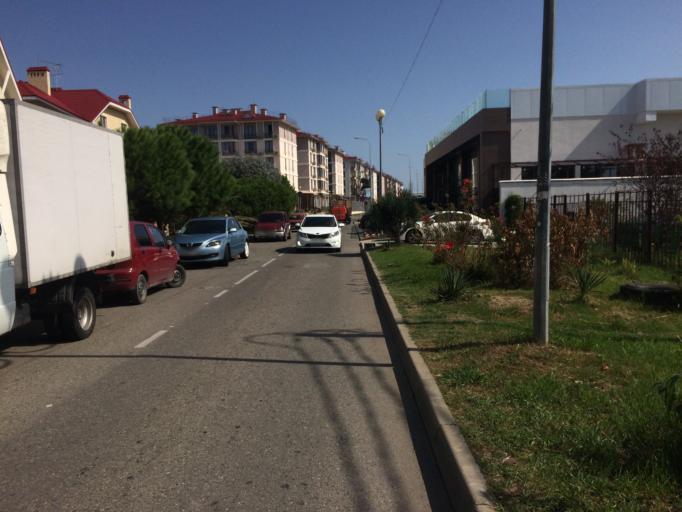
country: RU
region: Krasnodarskiy
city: Adler
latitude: 43.3971
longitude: 39.9732
